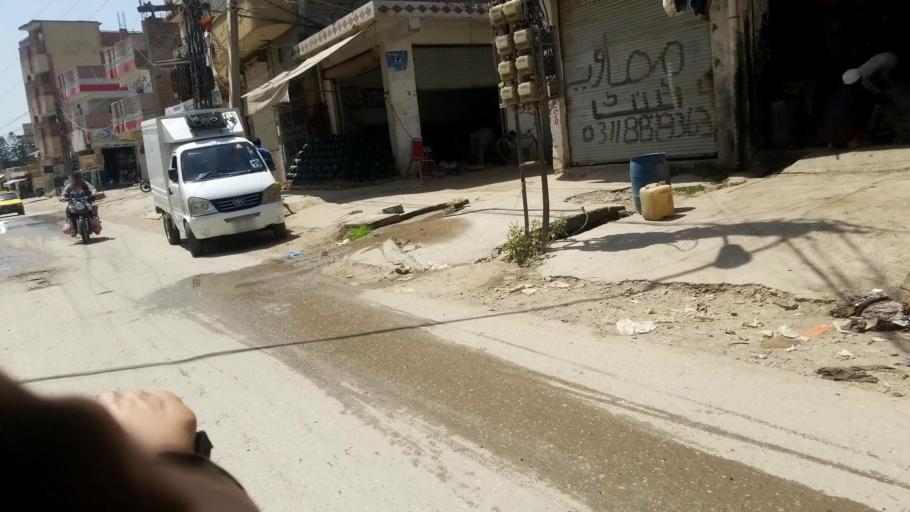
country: PK
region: Khyber Pakhtunkhwa
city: Peshawar
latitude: 34.0253
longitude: 71.4869
